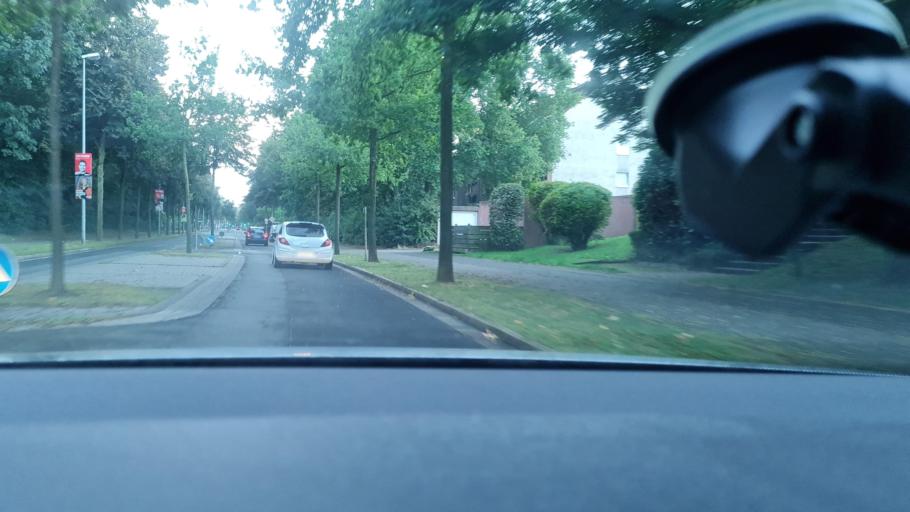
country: DE
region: North Rhine-Westphalia
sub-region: Regierungsbezirk Dusseldorf
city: Moers
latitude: 51.4873
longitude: 6.6166
